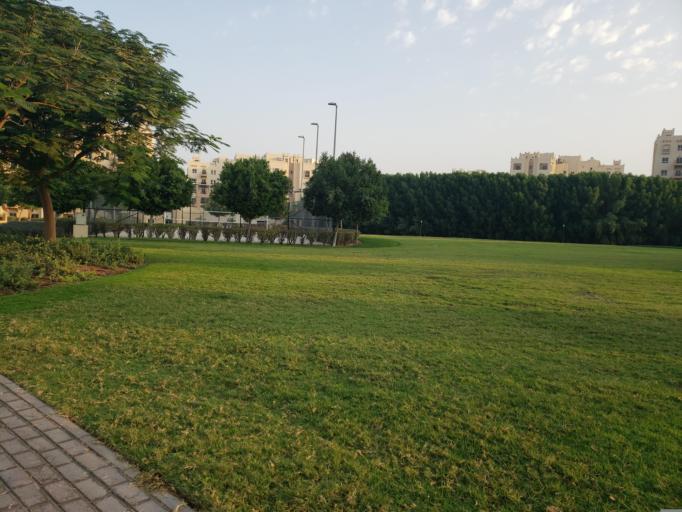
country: AE
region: Dubai
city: Dubai
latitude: 25.0017
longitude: 55.2538
